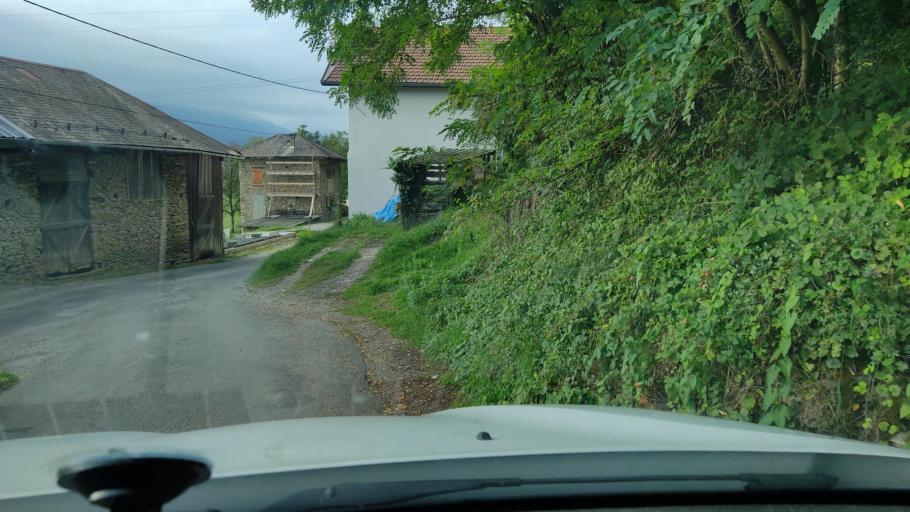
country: FR
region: Rhone-Alpes
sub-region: Departement de la Savoie
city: La Rochette
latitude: 45.4780
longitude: 6.1175
